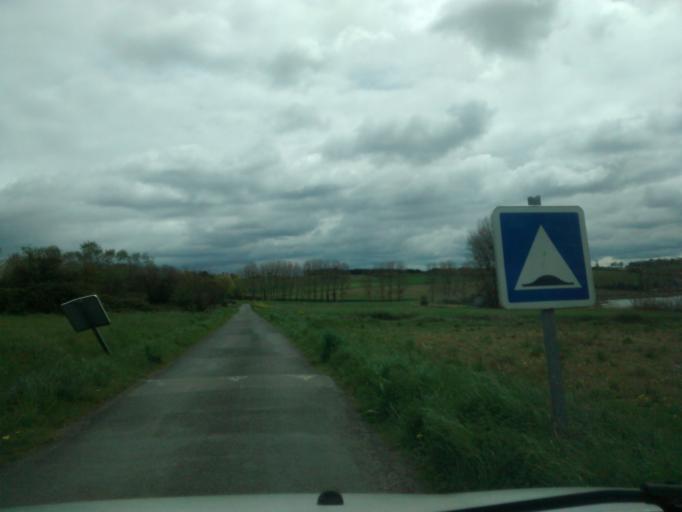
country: FR
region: Brittany
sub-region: Departement d'Ille-et-Vilaine
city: Saint-Jouan-des-Guerets
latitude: 48.5812
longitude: -1.9586
